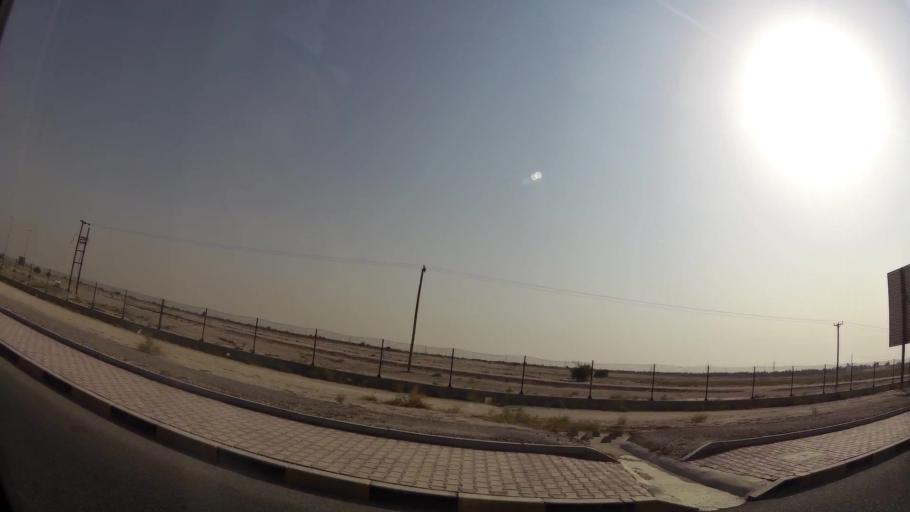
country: KW
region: Al Asimah
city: Ar Rabiyah
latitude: 29.2952
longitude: 47.7993
